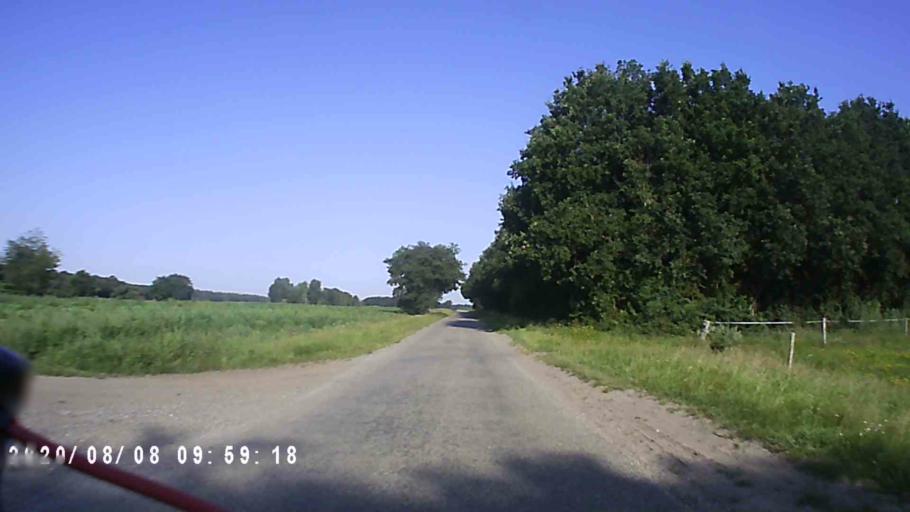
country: NL
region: Groningen
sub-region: Gemeente Leek
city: Leek
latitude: 53.1003
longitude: 6.4043
